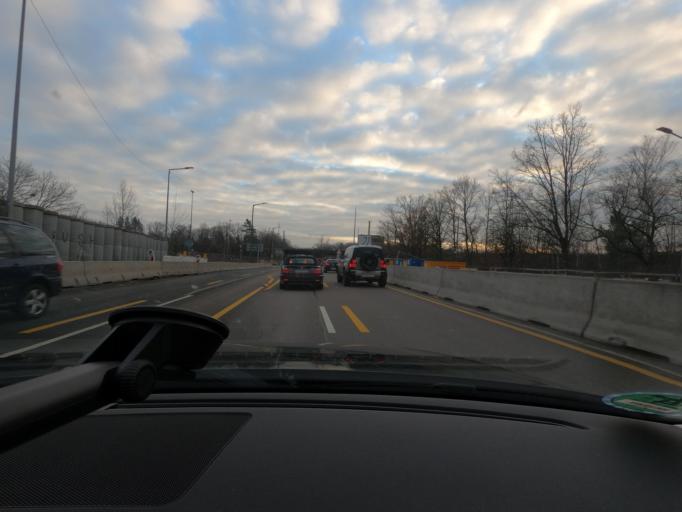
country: DE
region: Bavaria
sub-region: Regierungsbezirk Mittelfranken
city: Nuernberg
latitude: 49.4073
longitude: 11.1141
